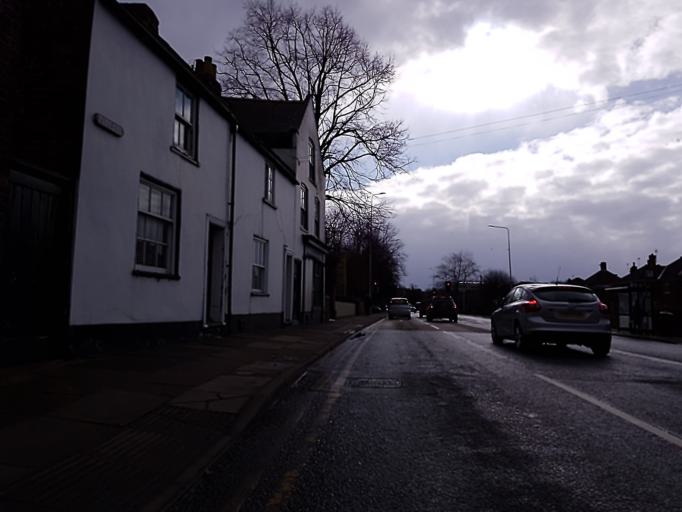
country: GB
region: England
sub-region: North East Lincolnshire
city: Grimbsy
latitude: 53.5582
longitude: -0.0916
